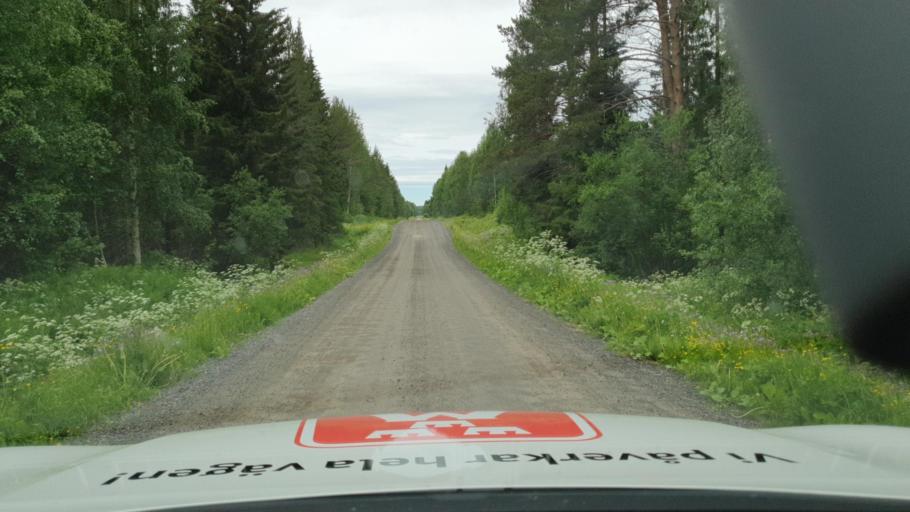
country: SE
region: Vaesterbotten
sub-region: Skelleftea Kommun
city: Burtraesk
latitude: 64.3949
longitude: 20.5872
